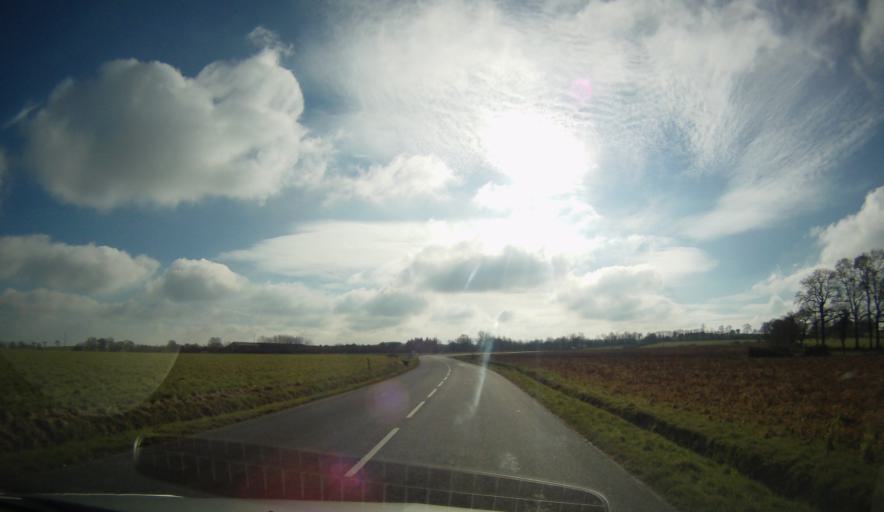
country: FR
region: Brittany
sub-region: Departement d'Ille-et-Vilaine
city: Corps-Nuds
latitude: 47.9452
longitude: -1.5608
